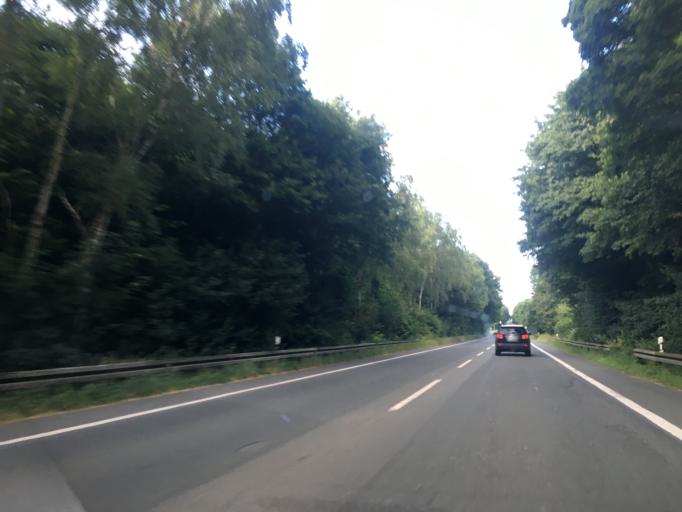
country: DE
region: North Rhine-Westphalia
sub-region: Regierungsbezirk Munster
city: Haltern
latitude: 51.7822
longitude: 7.2121
